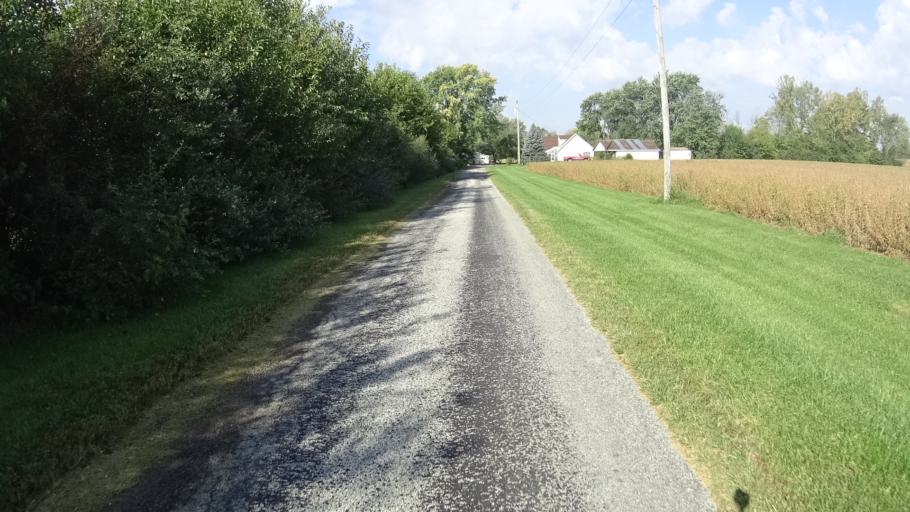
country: US
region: Indiana
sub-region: Madison County
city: Ingalls
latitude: 39.9927
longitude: -85.8325
